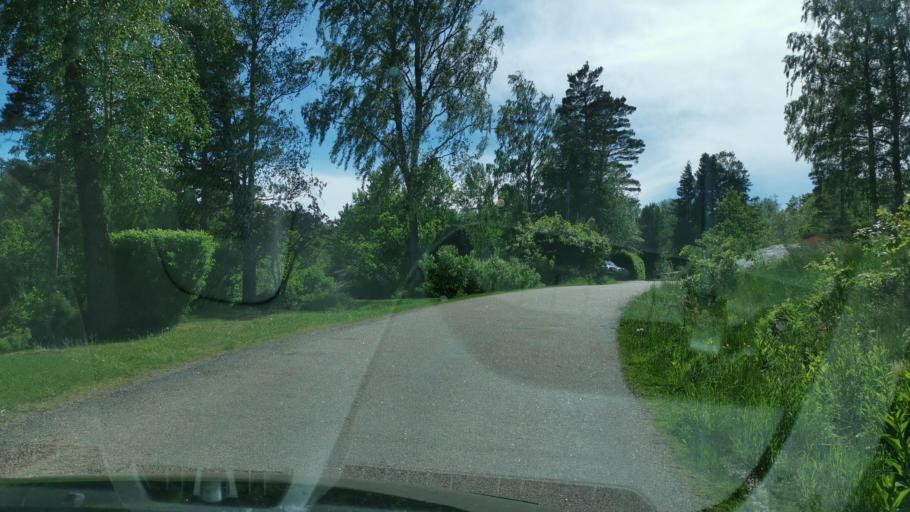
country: SE
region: Vaestra Goetaland
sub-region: Orust
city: Henan
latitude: 58.2690
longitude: 11.6368
